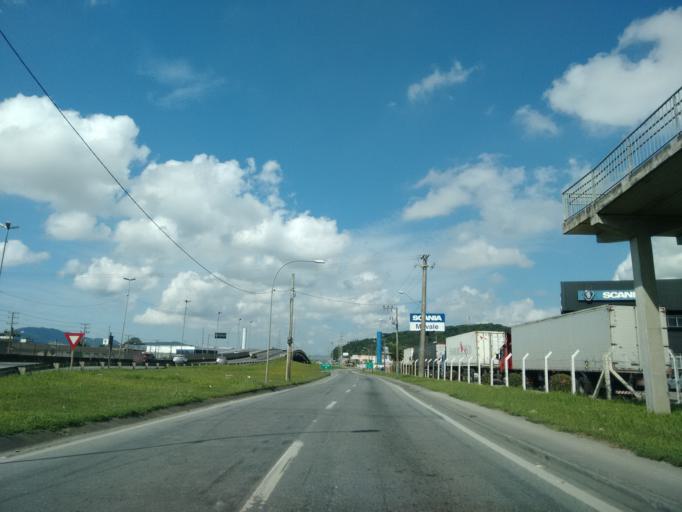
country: BR
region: Santa Catarina
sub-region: Itajai
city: Itajai
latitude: -26.8879
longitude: -48.7226
